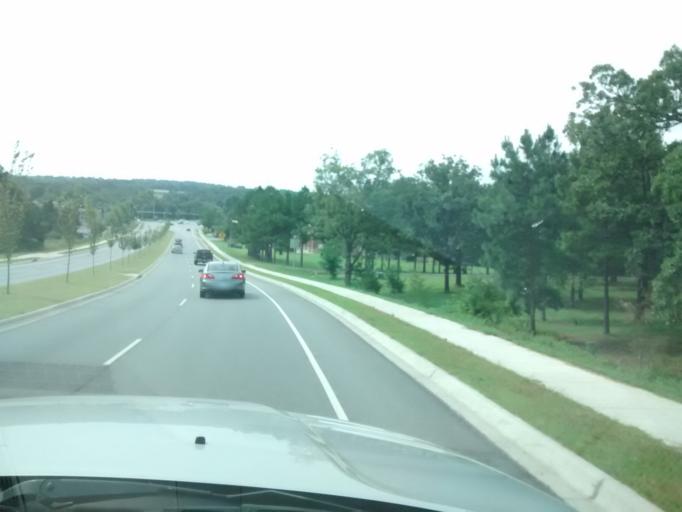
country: US
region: Arkansas
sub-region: Washington County
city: Johnson
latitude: 36.1230
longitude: -94.1208
